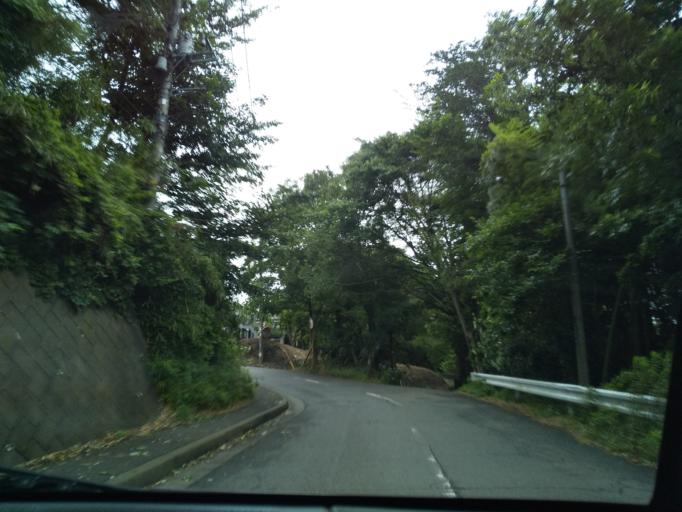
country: JP
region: Kanagawa
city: Minami-rinkan
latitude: 35.4289
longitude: 139.4434
